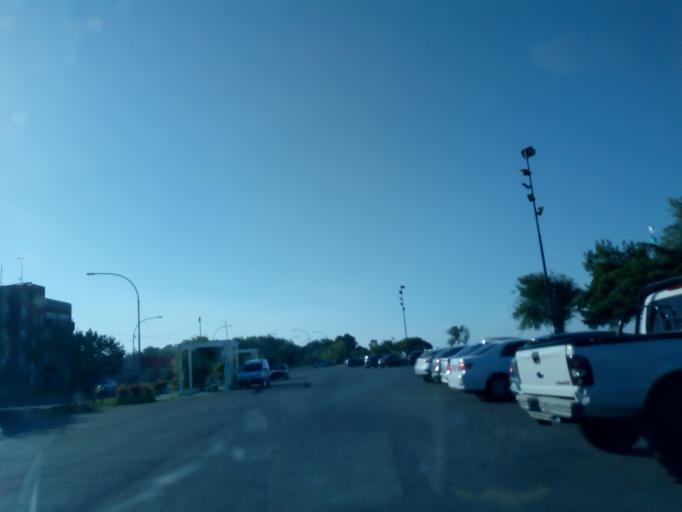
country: AR
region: Buenos Aires
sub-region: Partido de Ensenada
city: Ensenada
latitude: -34.8064
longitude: -57.9834
